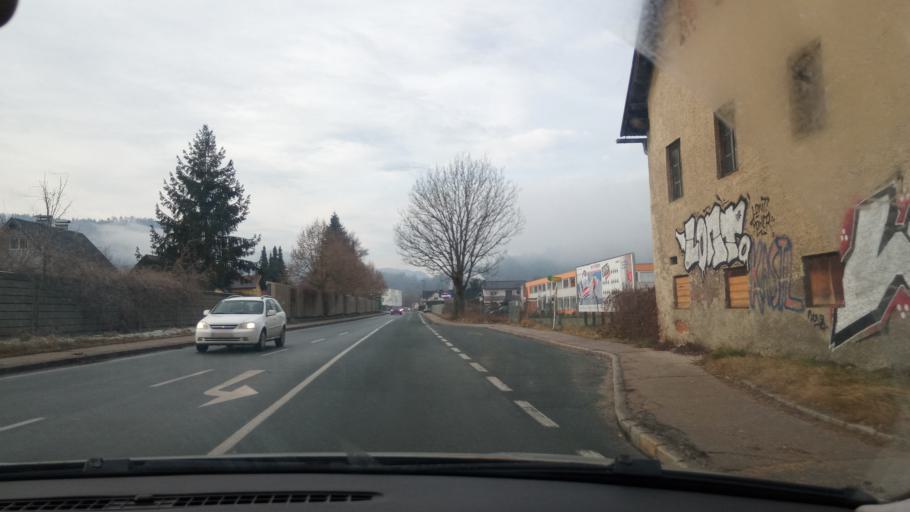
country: AT
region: Carinthia
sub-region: Klagenfurt am Woerthersee
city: Klagenfurt am Woerthersee
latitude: 46.5924
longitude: 14.2790
